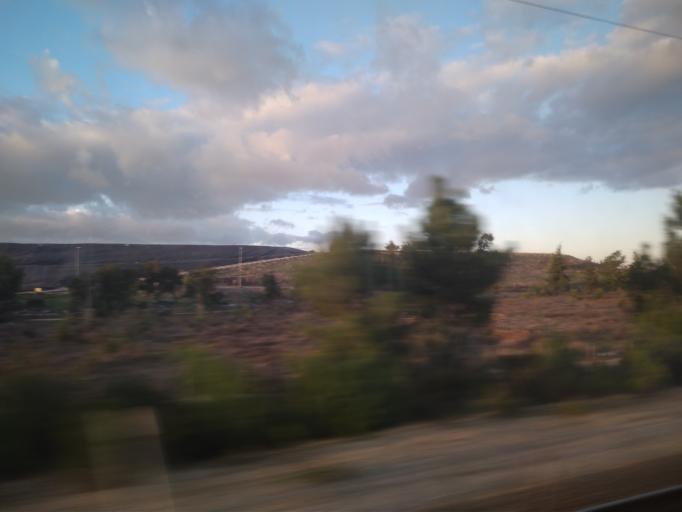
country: PT
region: Setubal
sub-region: Moita
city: Moita
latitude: 38.6079
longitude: -8.9743
